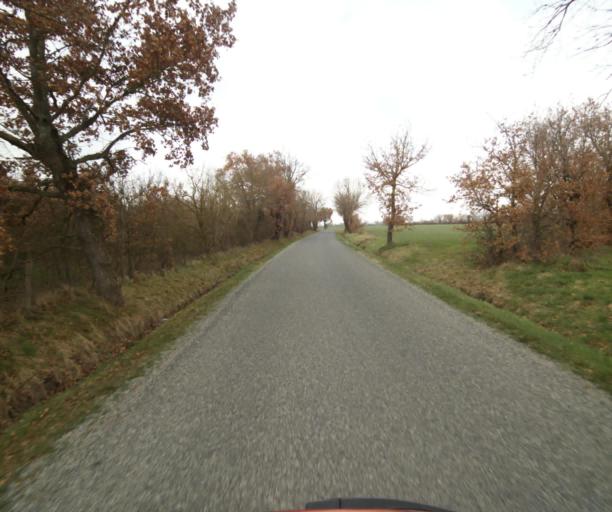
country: FR
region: Languedoc-Roussillon
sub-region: Departement de l'Aude
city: Belpech
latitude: 43.1864
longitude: 1.7018
